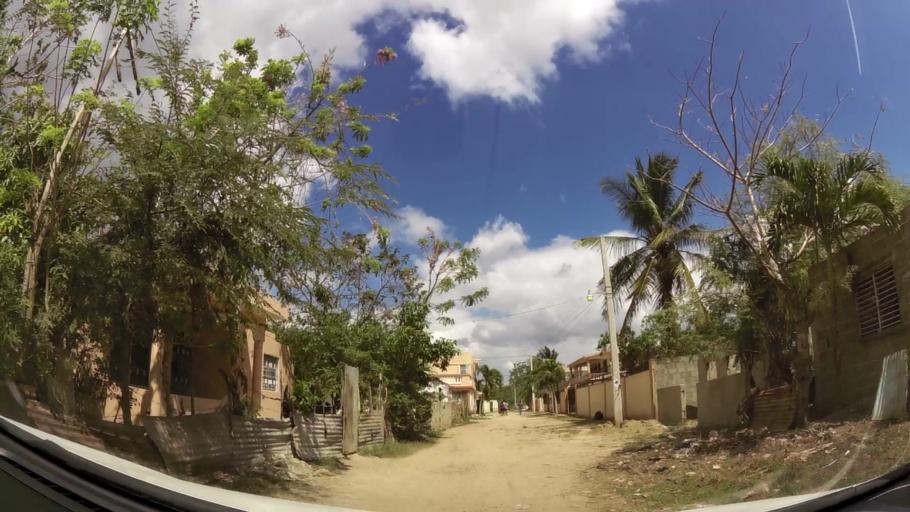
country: DO
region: Santo Domingo
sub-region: Santo Domingo
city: Boca Chica
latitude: 18.4511
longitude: -69.6509
